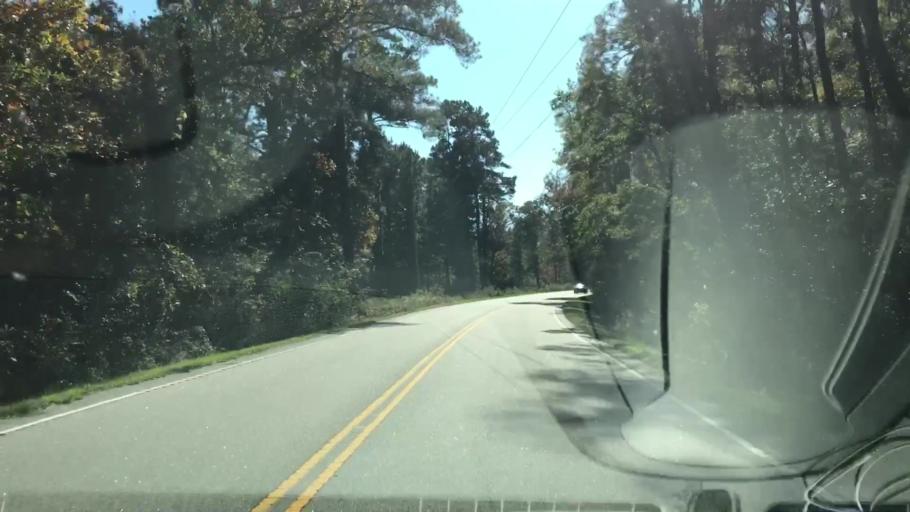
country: US
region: South Carolina
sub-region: Jasper County
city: Ridgeland
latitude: 32.4809
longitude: -80.8836
